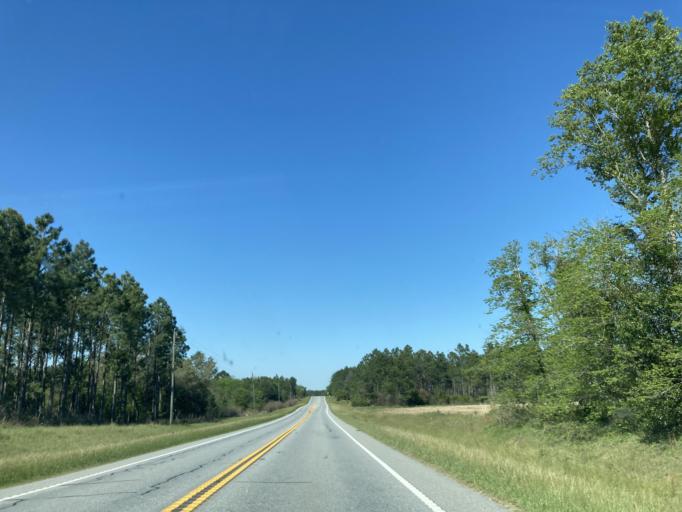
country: US
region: Georgia
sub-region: Baker County
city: Newton
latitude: 31.2381
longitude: -84.4359
